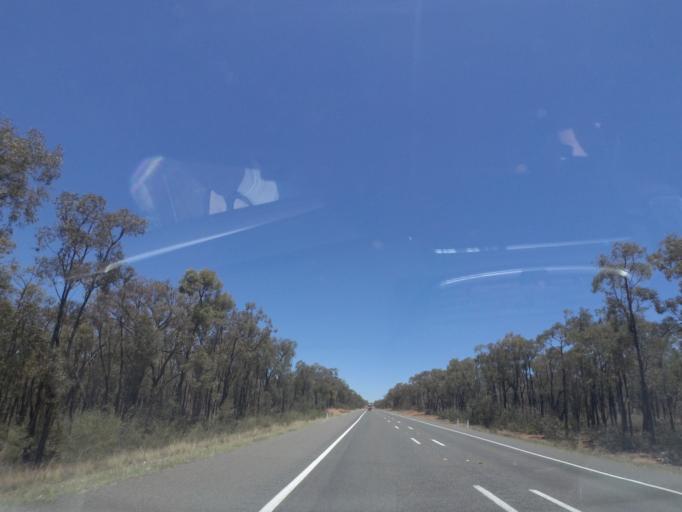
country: AU
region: New South Wales
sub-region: Warrumbungle Shire
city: Coonabarabran
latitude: -30.9083
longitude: 149.4369
